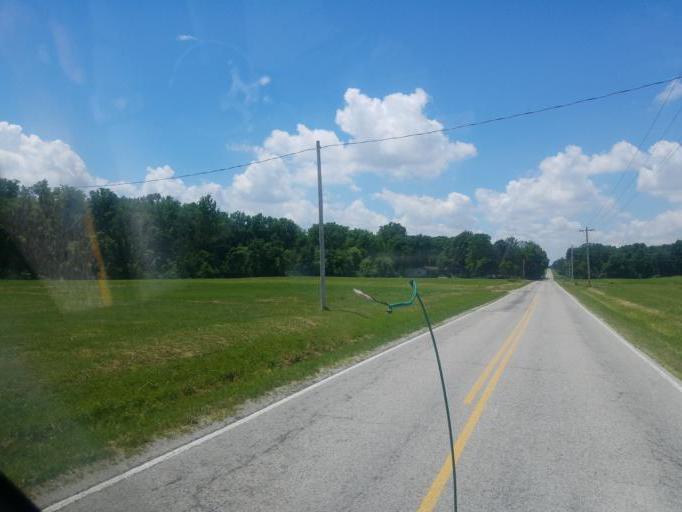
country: US
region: Ohio
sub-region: Huron County
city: Plymouth
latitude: 41.0679
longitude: -82.6205
